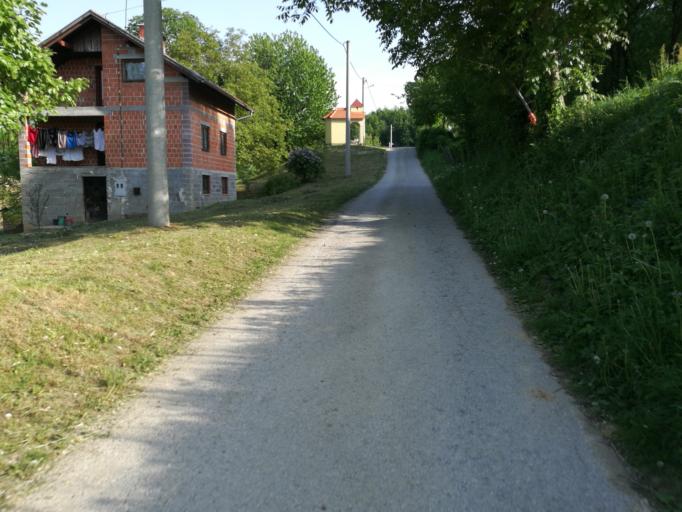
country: HR
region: Krapinsko-Zagorska
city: Radoboj
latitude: 46.2325
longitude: 15.9084
